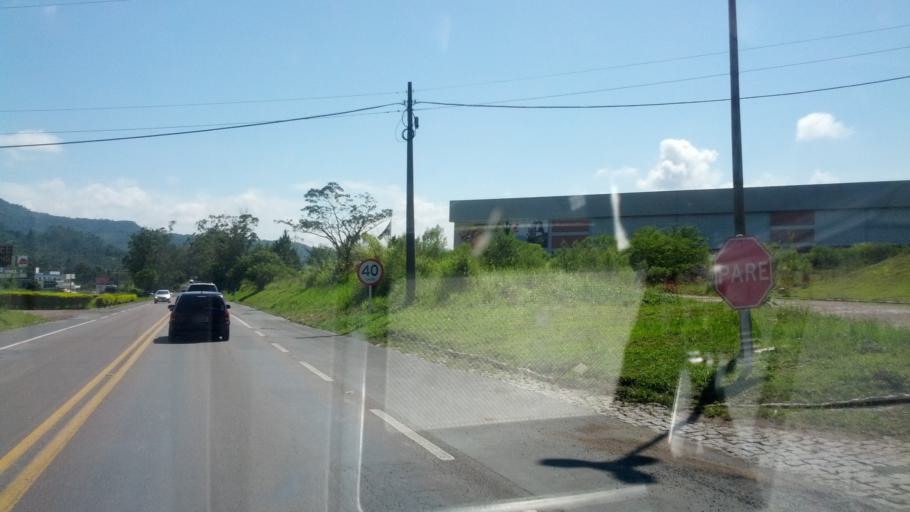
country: BR
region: Santa Catarina
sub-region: Rio Do Sul
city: Rio do Sul
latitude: -27.1820
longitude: -49.6003
